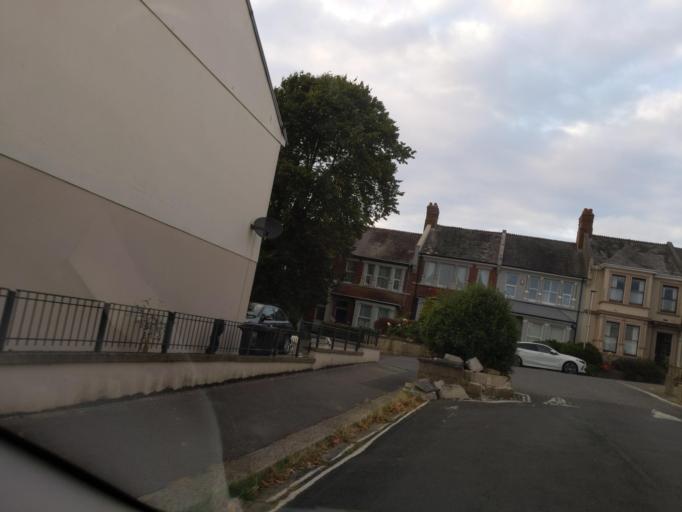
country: GB
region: England
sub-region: Cornwall
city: Millbrook
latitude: 50.3799
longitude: -4.1770
